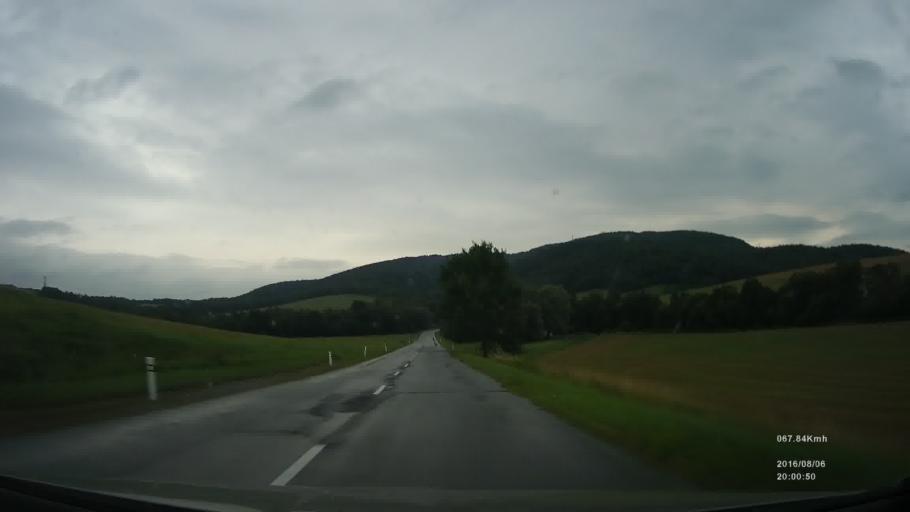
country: SK
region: Presovsky
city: Svidnik
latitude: 49.2485
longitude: 21.5834
